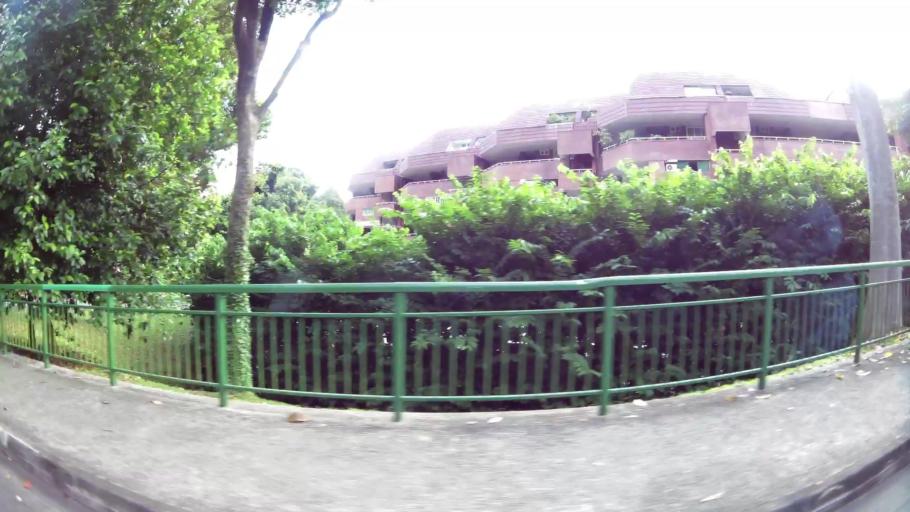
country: SG
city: Singapore
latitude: 1.2692
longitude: 103.8242
